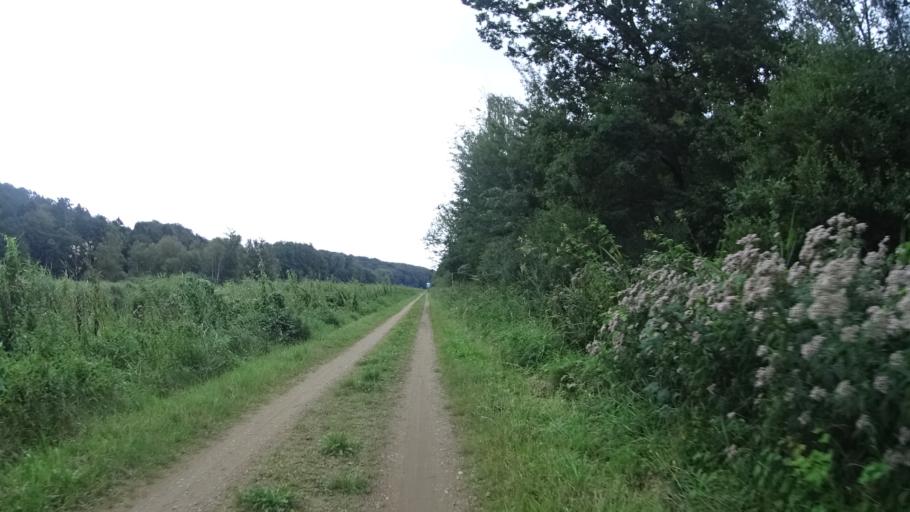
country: DE
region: Schleswig-Holstein
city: Alt Molln
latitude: 53.6412
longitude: 10.6559
